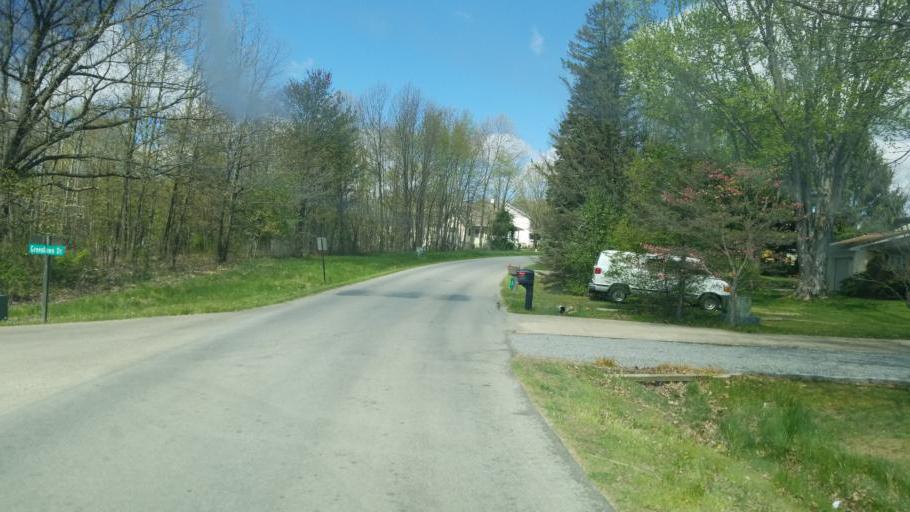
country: US
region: Ohio
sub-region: Knox County
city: Gambier
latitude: 40.4402
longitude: -82.3604
